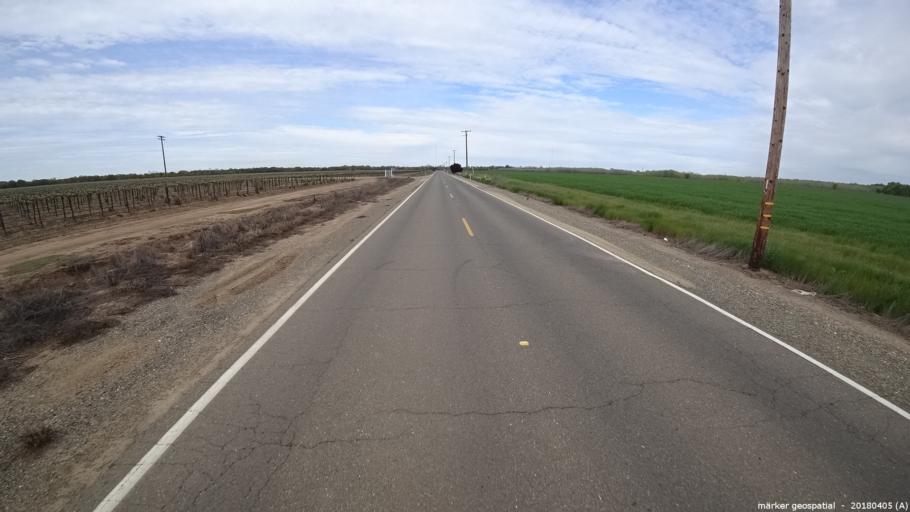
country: US
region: California
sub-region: San Joaquin County
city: Thornton
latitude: 38.2412
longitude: -121.3929
